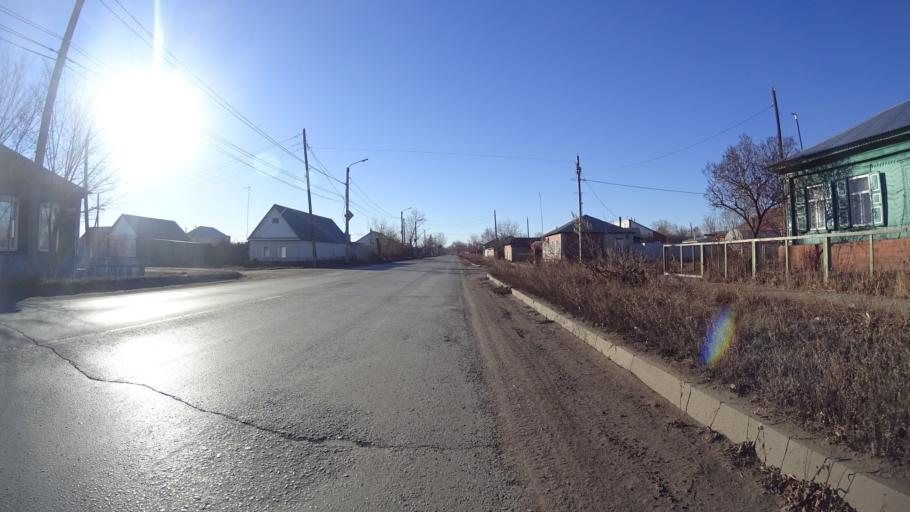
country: RU
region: Chelyabinsk
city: Troitsk
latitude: 54.1095
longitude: 61.5643
